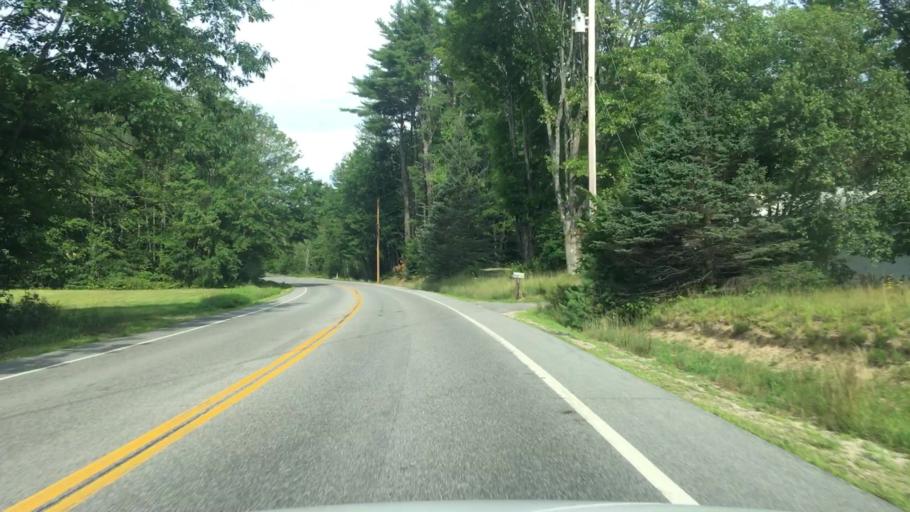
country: US
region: New Hampshire
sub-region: Carroll County
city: Effingham
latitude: 43.7944
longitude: -70.9831
